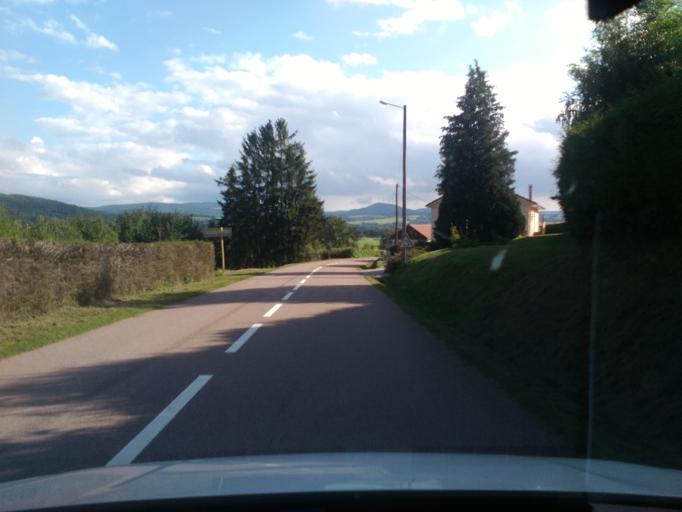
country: FR
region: Lorraine
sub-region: Departement des Vosges
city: Corcieux
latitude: 48.2030
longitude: 6.8836
